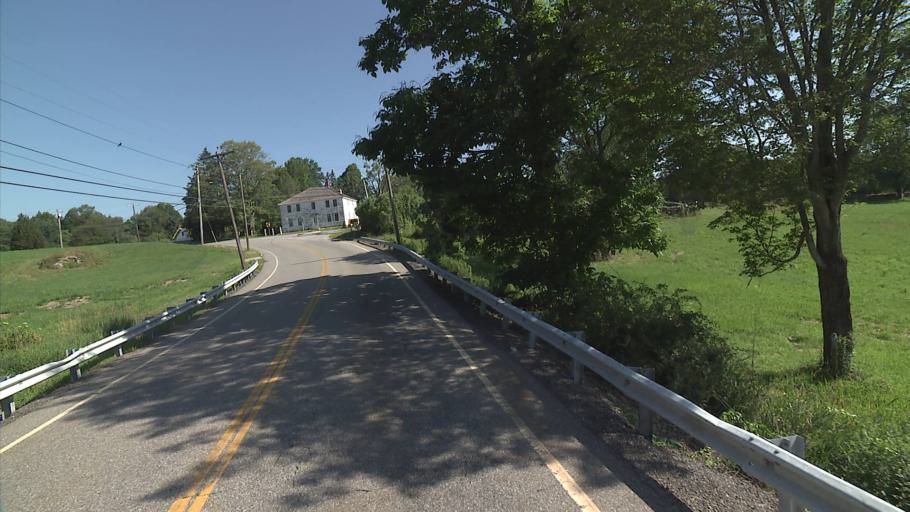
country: US
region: Connecticut
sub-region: New London County
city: Montville Center
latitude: 41.4825
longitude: -72.1614
